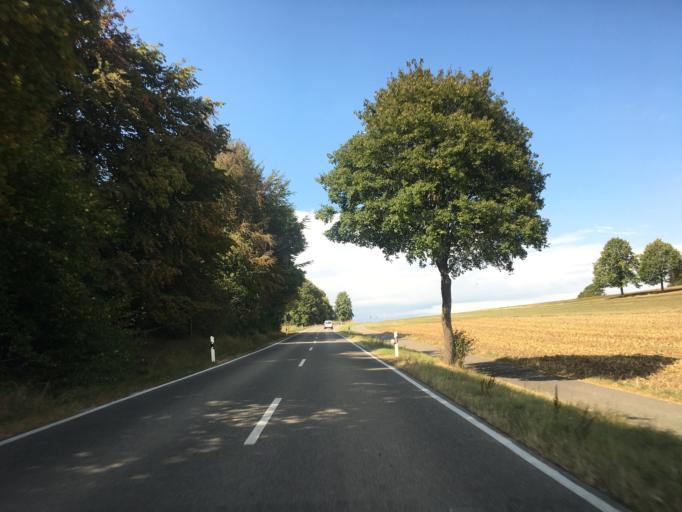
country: DE
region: Baden-Wuerttemberg
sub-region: Tuebingen Region
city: Trochtelfingen
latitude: 48.3802
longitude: 9.1948
